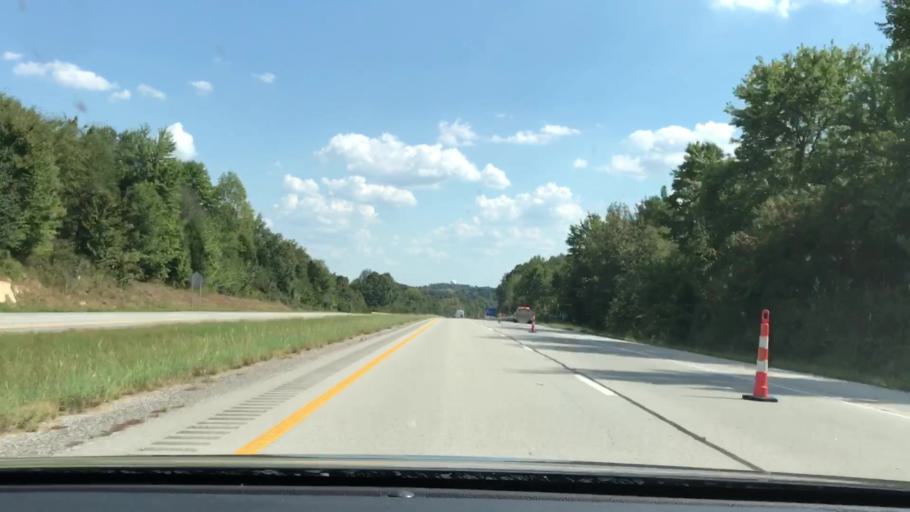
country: US
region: Kentucky
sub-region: Butler County
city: Morgantown
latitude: 37.2248
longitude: -86.7198
